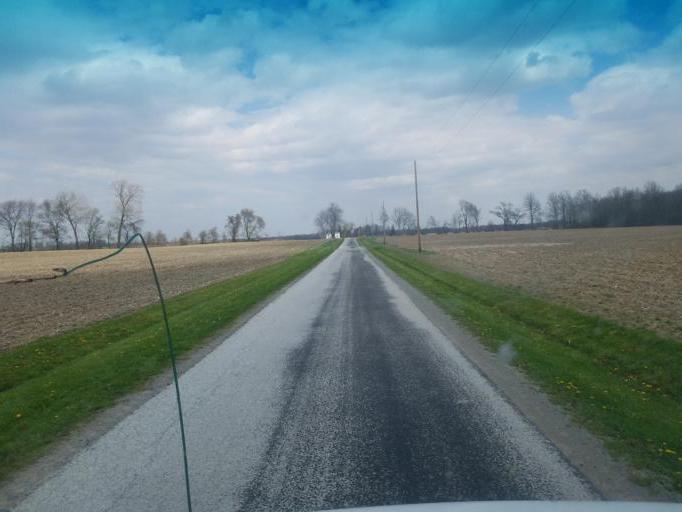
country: US
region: Ohio
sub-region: Wyandot County
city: Upper Sandusky
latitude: 40.9414
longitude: -83.2337
